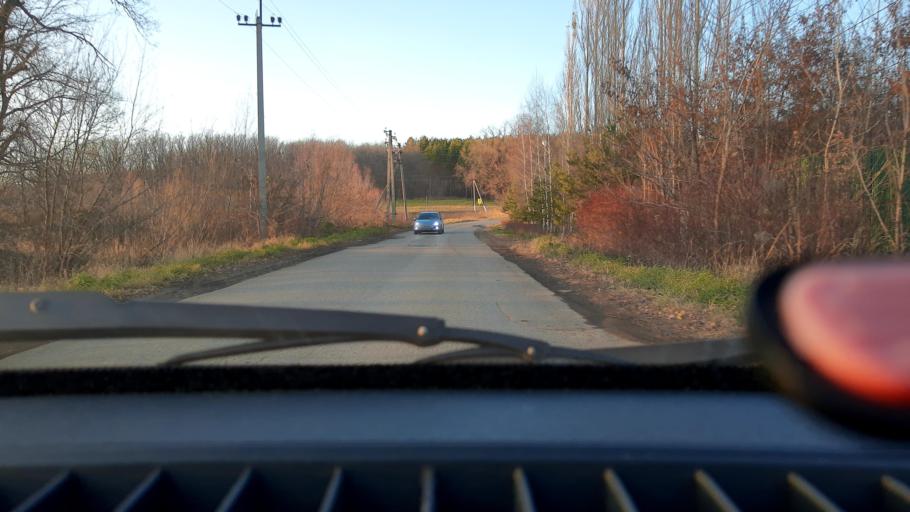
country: RU
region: Bashkortostan
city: Mikhaylovka
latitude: 54.8050
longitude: 55.8778
